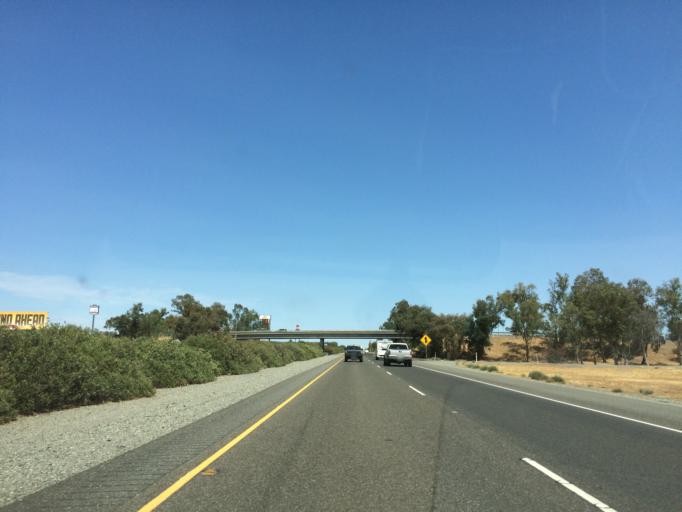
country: US
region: California
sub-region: Glenn County
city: Orland
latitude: 39.7486
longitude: -122.2054
